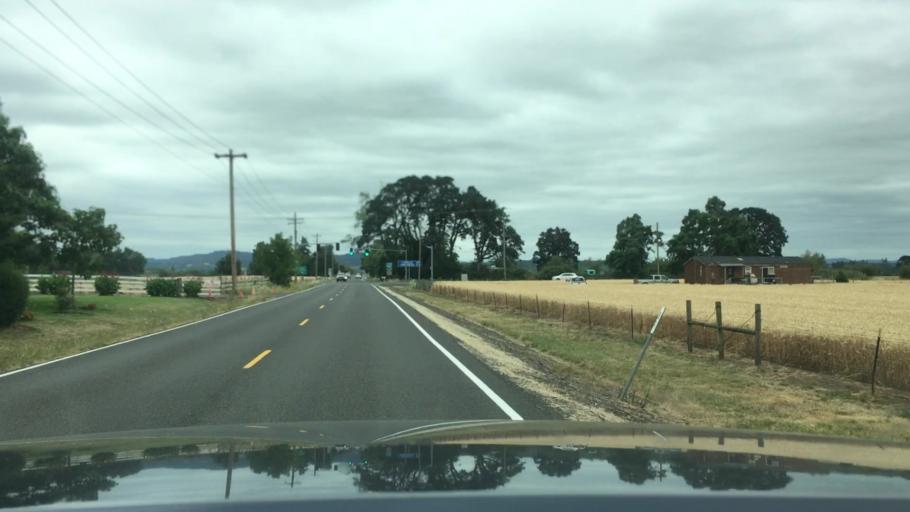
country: US
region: Oregon
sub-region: Lane County
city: Junction City
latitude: 44.1043
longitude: -123.2084
